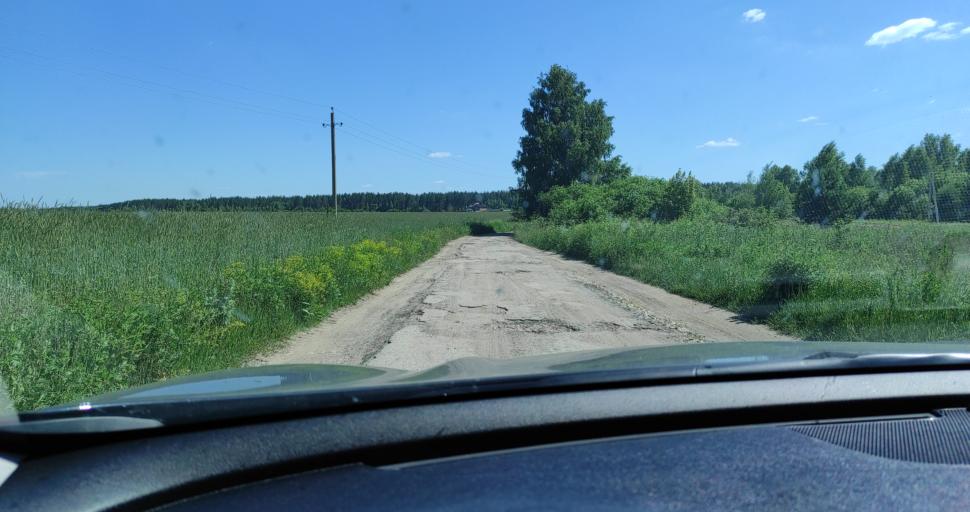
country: RU
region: Rjazan
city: Murmino
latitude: 54.5666
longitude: 40.0958
